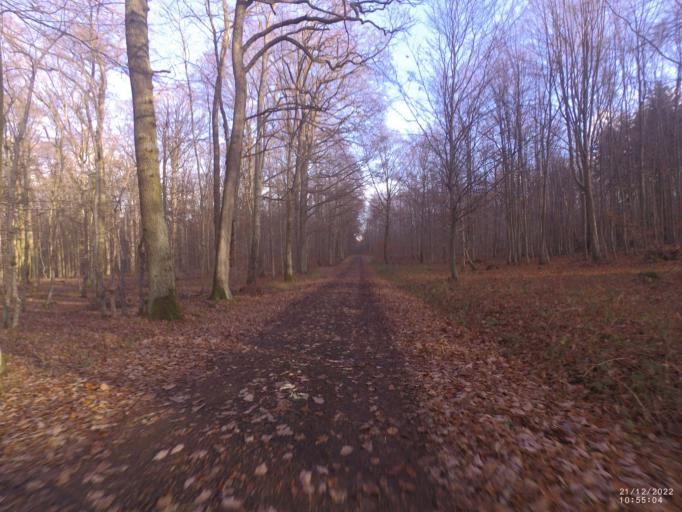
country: DE
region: Rheinland-Pfalz
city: Konigsfeld
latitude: 50.4984
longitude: 7.1978
